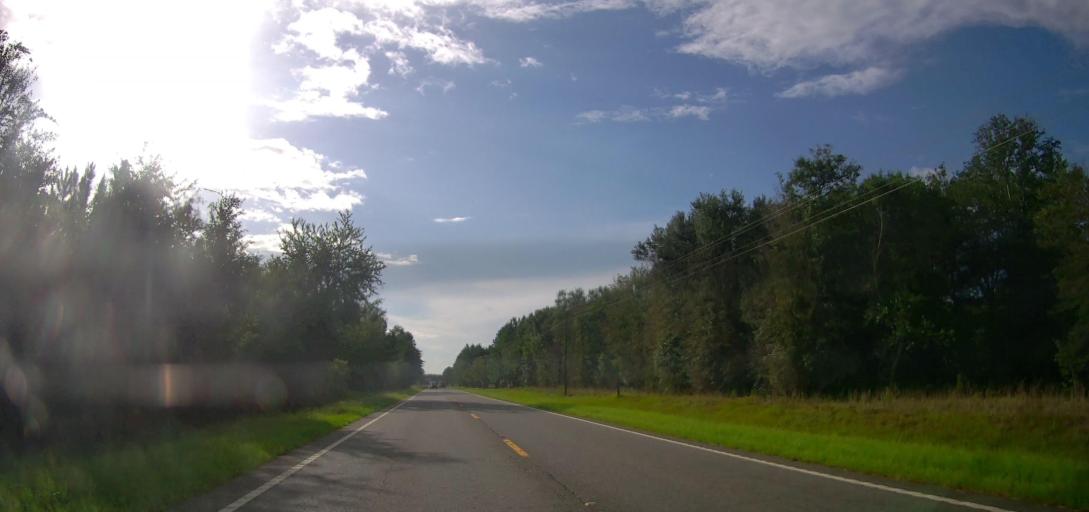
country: US
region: Georgia
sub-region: Coffee County
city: Nicholls
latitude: 31.3359
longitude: -82.5952
